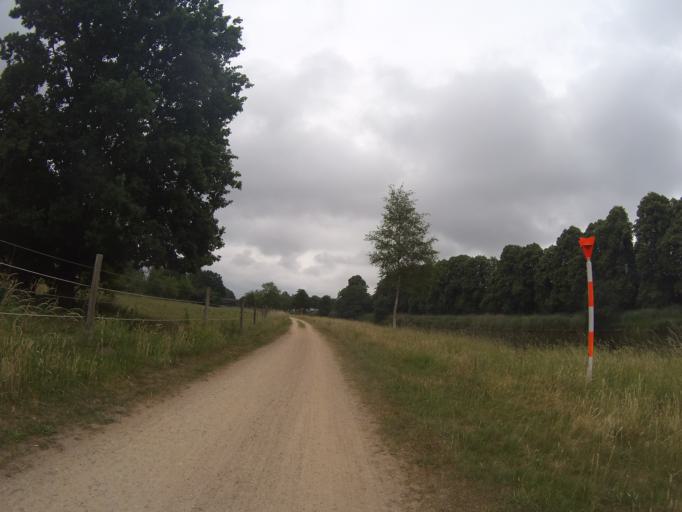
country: DE
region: Lower Saxony
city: Meppen
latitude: 52.7023
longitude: 7.2836
